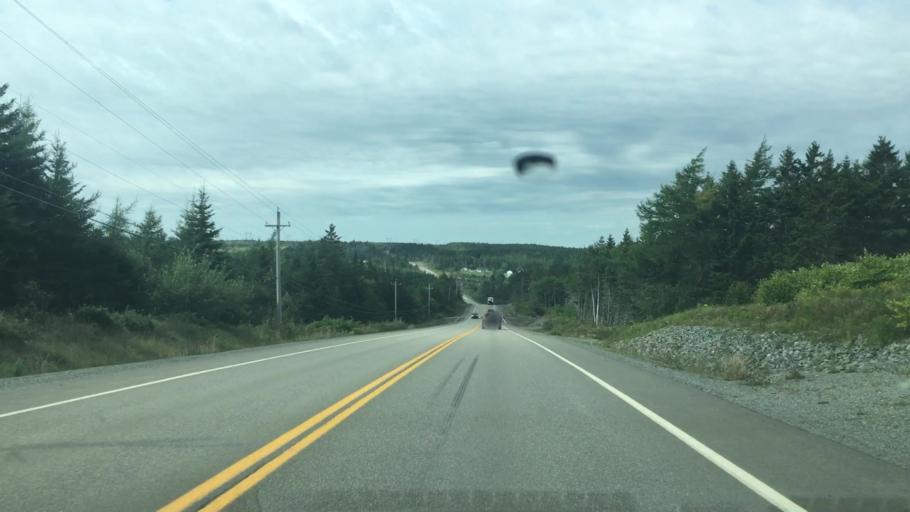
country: CA
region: Nova Scotia
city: Princeville
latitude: 45.6827
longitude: -60.7728
